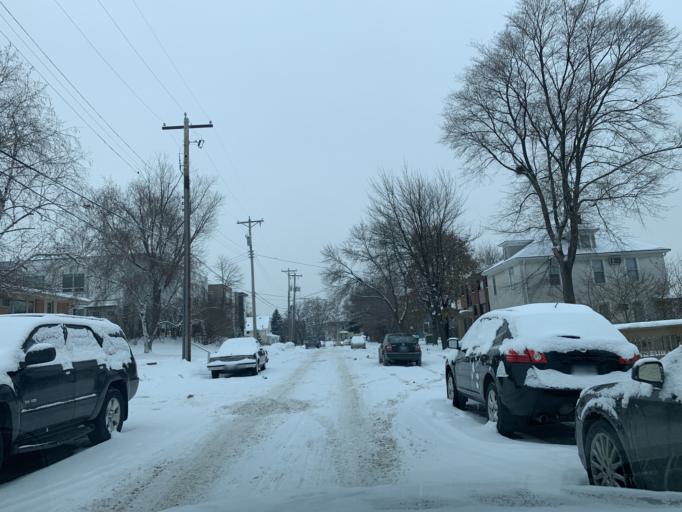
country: US
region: Minnesota
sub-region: Hennepin County
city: Saint Louis Park
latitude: 44.9467
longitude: -93.3305
